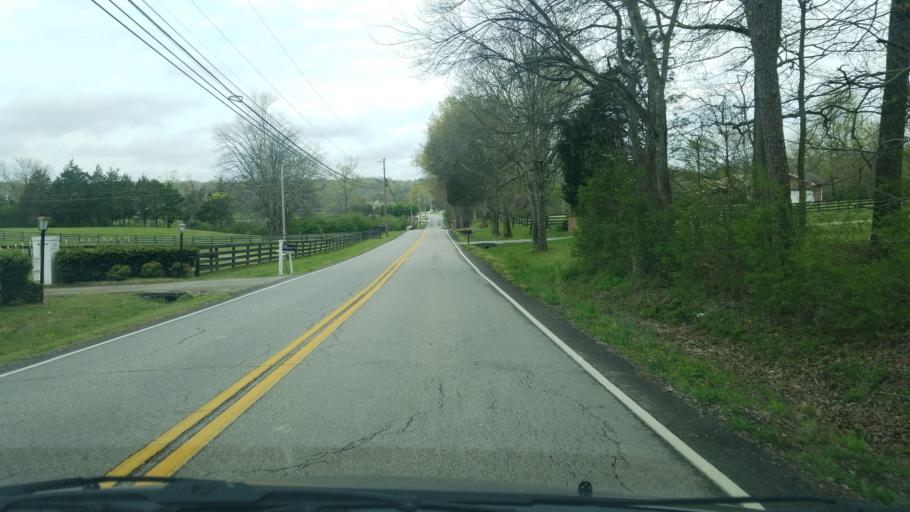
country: US
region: Tennessee
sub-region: Hamilton County
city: Collegedale
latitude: 35.0126
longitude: -85.0860
